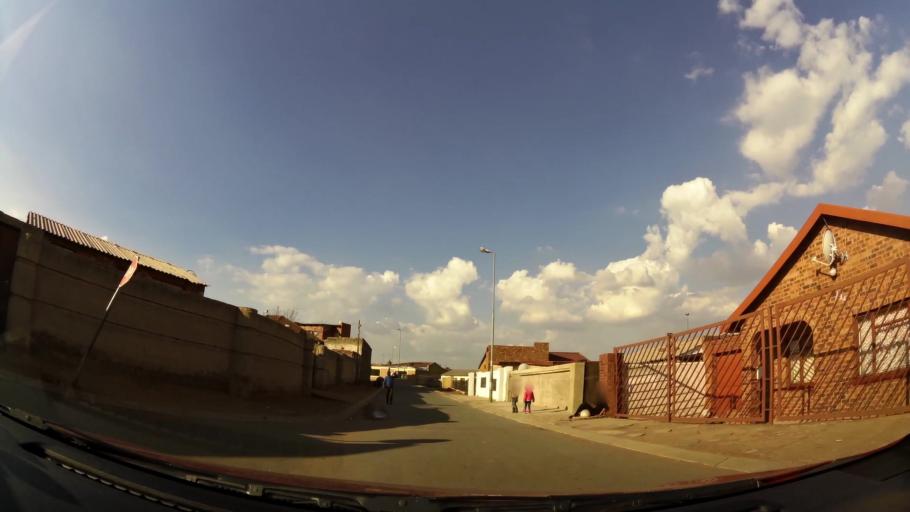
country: ZA
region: Gauteng
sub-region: City of Johannesburg Metropolitan Municipality
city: Soweto
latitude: -26.2346
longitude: 27.8629
